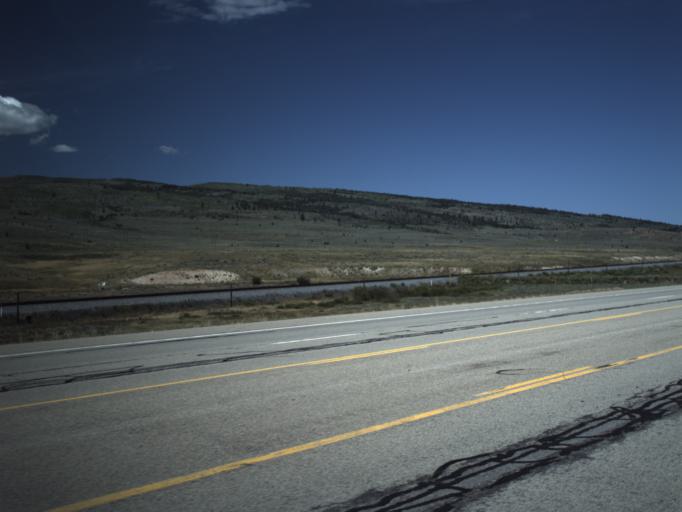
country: US
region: Utah
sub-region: Carbon County
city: Helper
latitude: 39.8714
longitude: -111.0330
